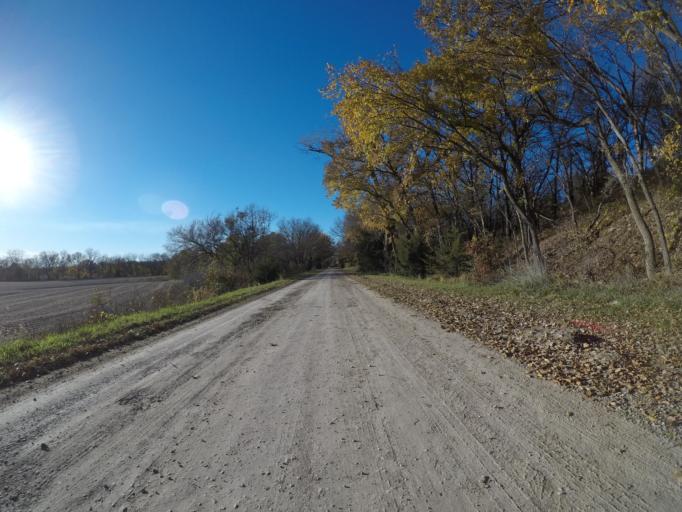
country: US
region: Kansas
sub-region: Riley County
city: Fort Riley North
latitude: 39.2638
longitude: -96.7794
